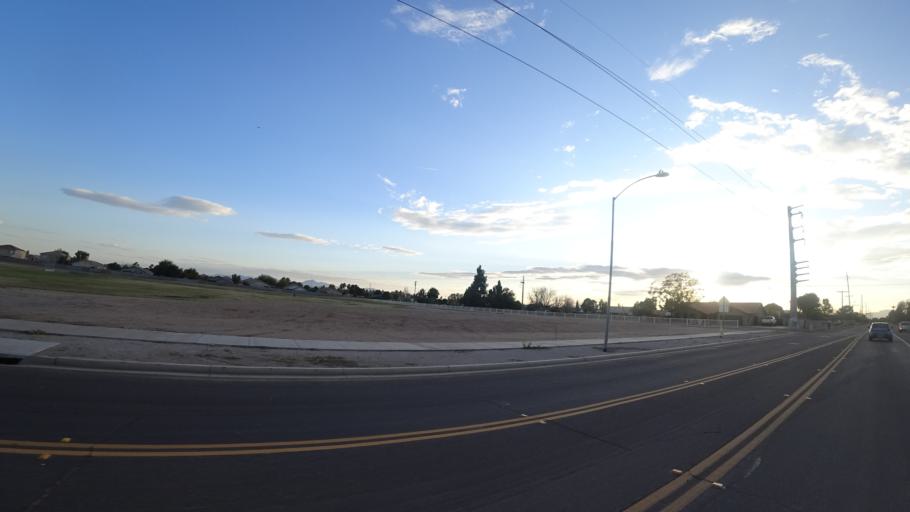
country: US
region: Arizona
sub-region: Maricopa County
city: Peoria
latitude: 33.5450
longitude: -112.2282
